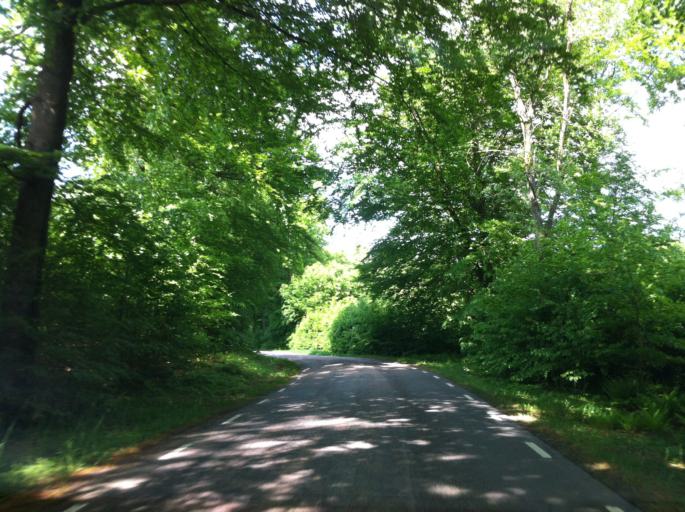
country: SE
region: Skane
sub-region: Svalovs Kommun
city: Kagerod
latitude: 56.0287
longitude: 13.1587
